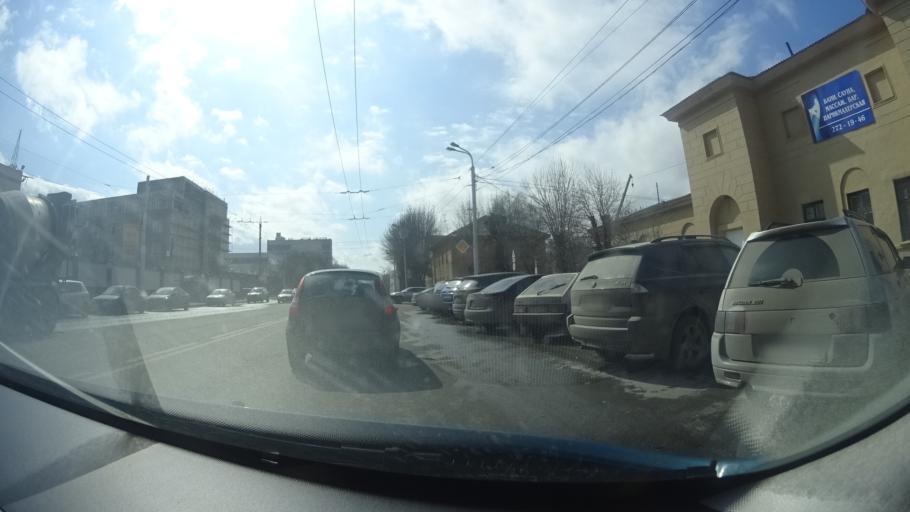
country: RU
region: Bashkortostan
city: Ufa
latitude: 54.7400
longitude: 55.9666
